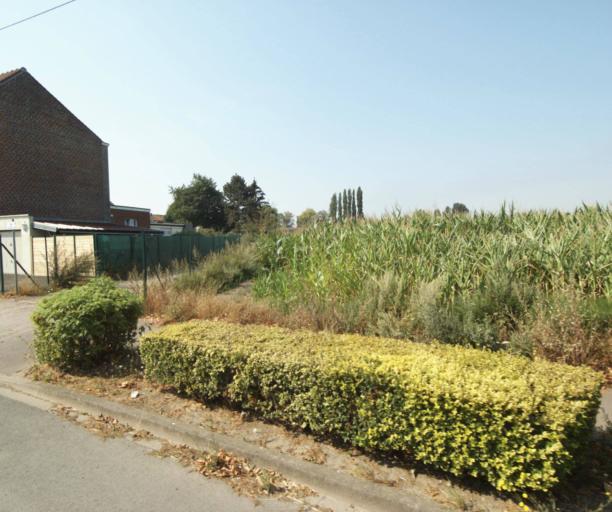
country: FR
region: Nord-Pas-de-Calais
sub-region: Departement du Nord
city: Quesnoy-sur-Deule
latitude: 50.7042
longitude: 3.0057
